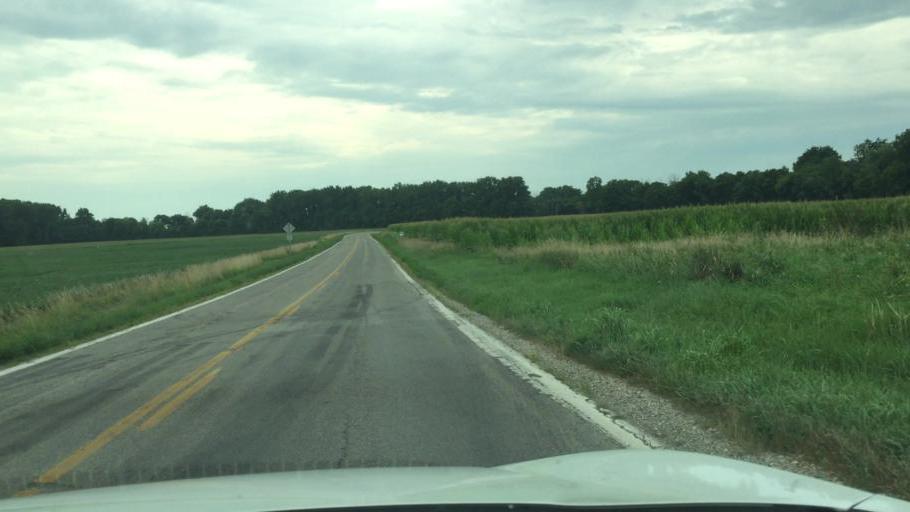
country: US
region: Ohio
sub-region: Champaign County
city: North Lewisburg
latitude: 40.2299
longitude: -83.5250
